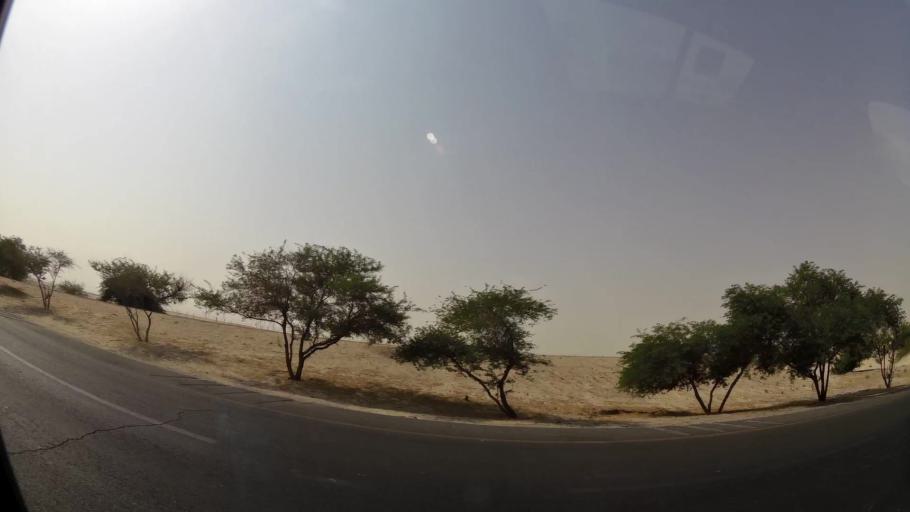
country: KW
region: Muhafazat al Jahra'
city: Al Jahra'
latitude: 29.3237
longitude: 47.6387
